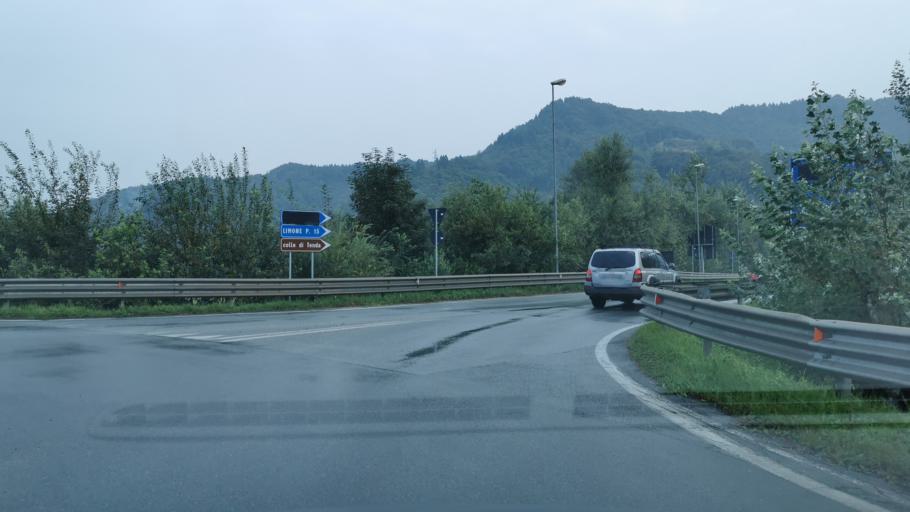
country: IT
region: Piedmont
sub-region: Provincia di Cuneo
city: Robilante
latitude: 44.3051
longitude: 7.5050
